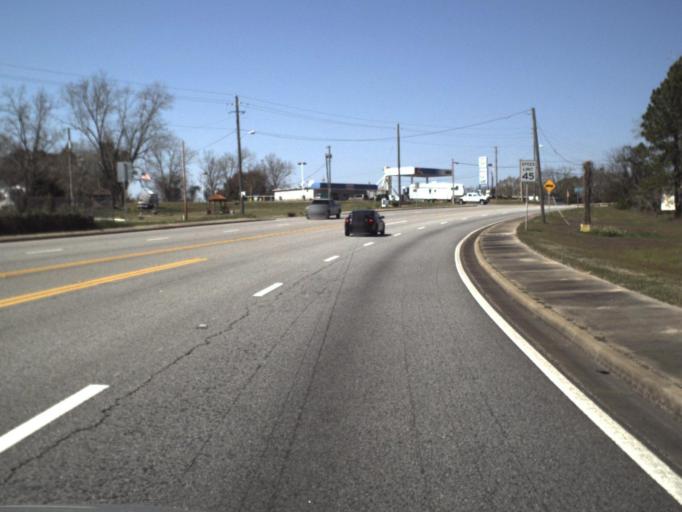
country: US
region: Florida
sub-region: Jackson County
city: Graceville
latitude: 30.9476
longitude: -85.4014
